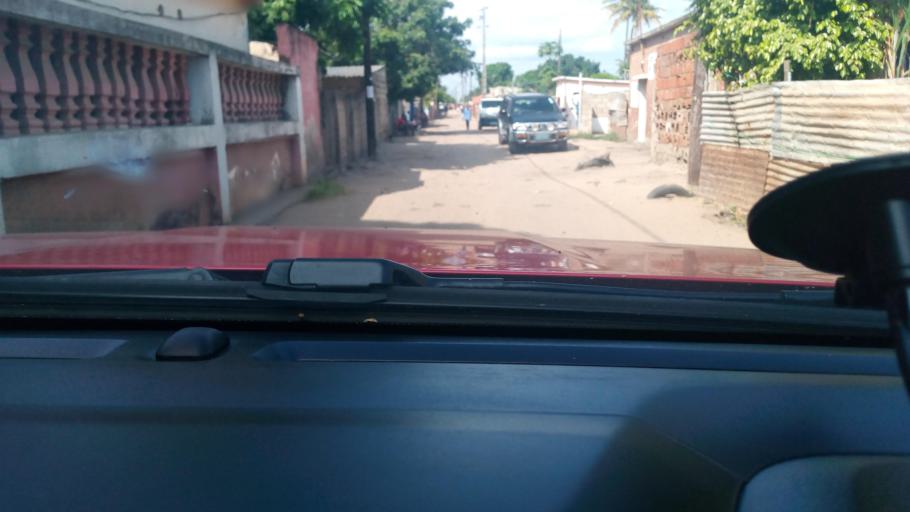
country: MZ
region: Maputo City
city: Maputo
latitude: -25.9145
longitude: 32.5632
